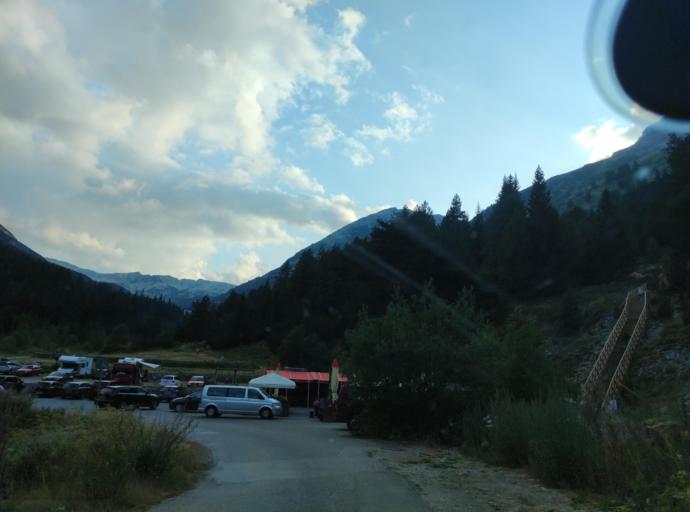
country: BG
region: Blagoevgrad
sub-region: Obshtina Bansko
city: Bansko
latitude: 41.7670
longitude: 23.4247
